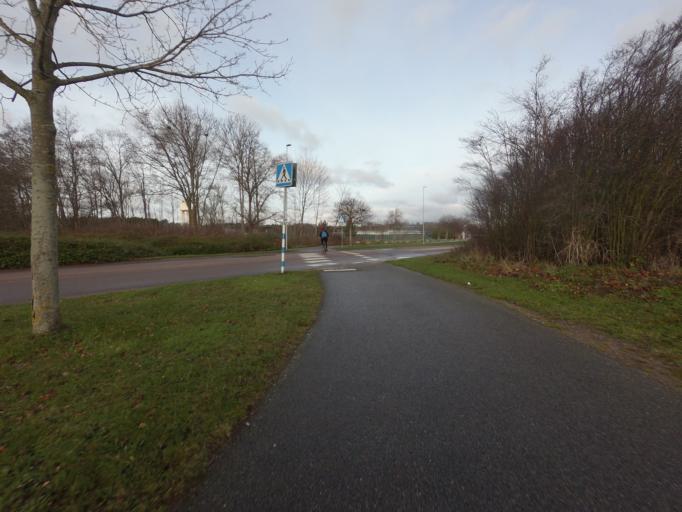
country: SE
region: Skane
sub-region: Hoganas Kommun
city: Hoganas
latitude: 56.1820
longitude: 12.5677
